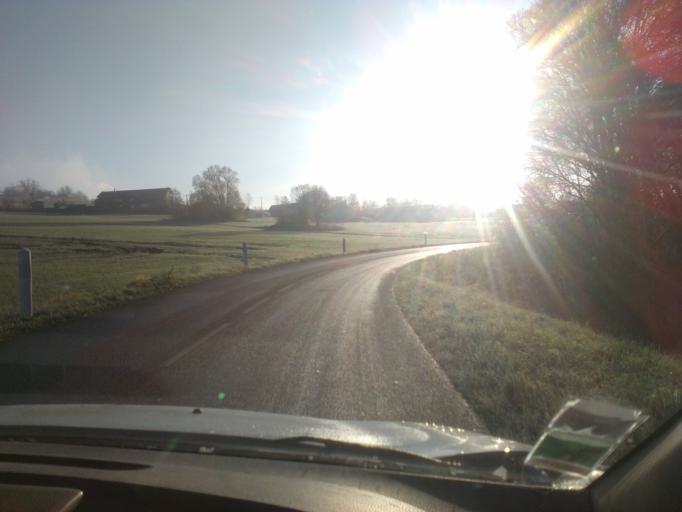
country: FR
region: Lorraine
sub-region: Departement des Vosges
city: Darnieulles
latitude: 48.1630
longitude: 6.2285
